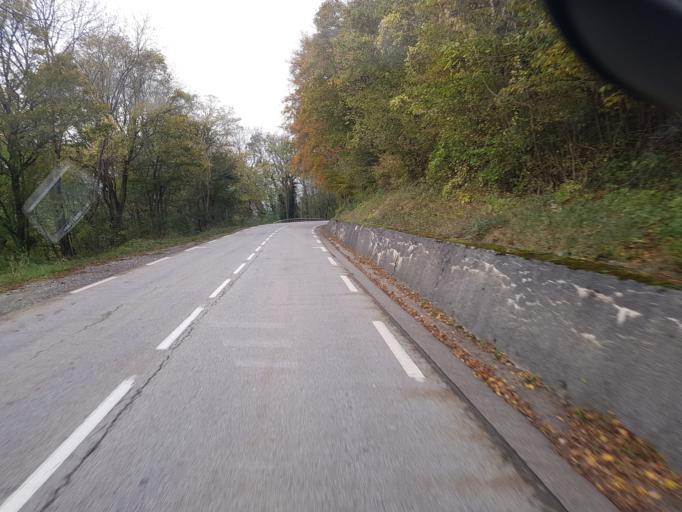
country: FR
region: Rhone-Alpes
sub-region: Departement de l'Isere
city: Le Gua
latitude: 44.9682
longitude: 5.6382
